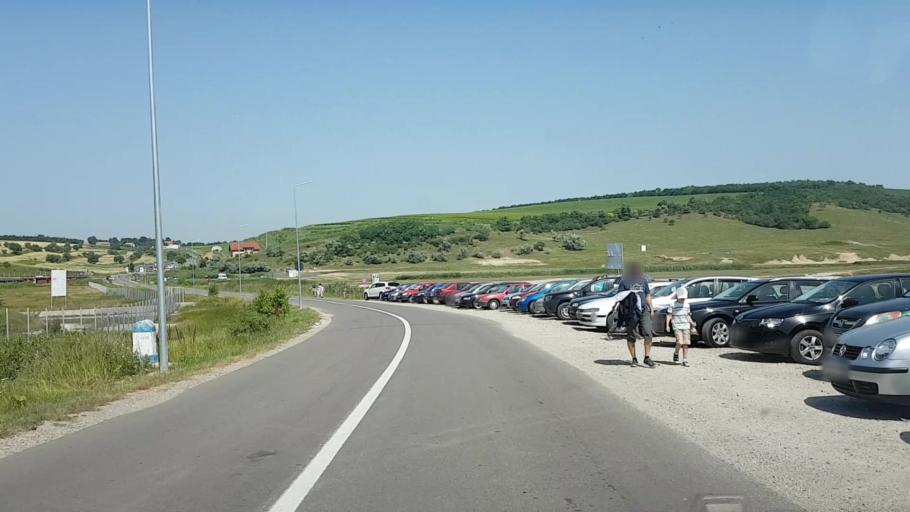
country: RO
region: Cluj
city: Turda
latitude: 46.5875
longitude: 23.7921
